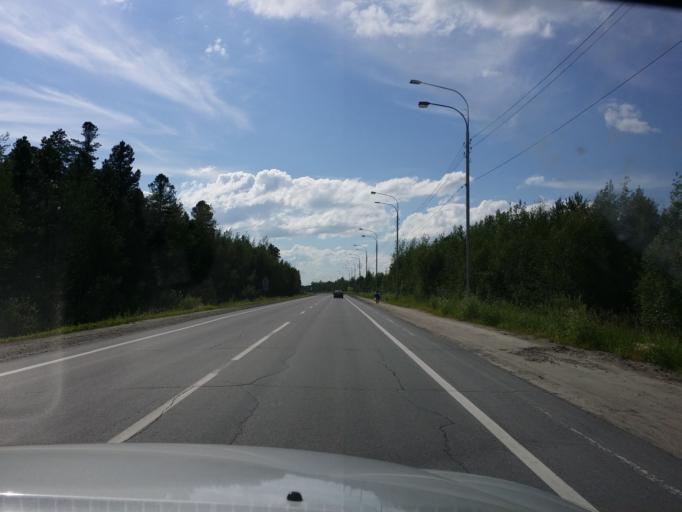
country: RU
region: Khanty-Mansiyskiy Avtonomnyy Okrug
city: Izluchinsk
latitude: 60.9651
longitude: 76.8466
